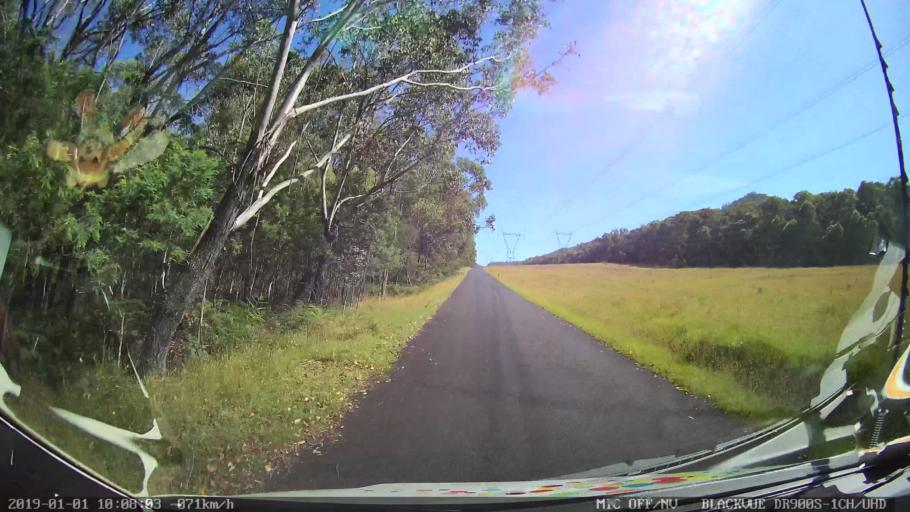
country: AU
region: New South Wales
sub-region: Snowy River
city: Jindabyne
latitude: -36.1632
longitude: 148.1573
